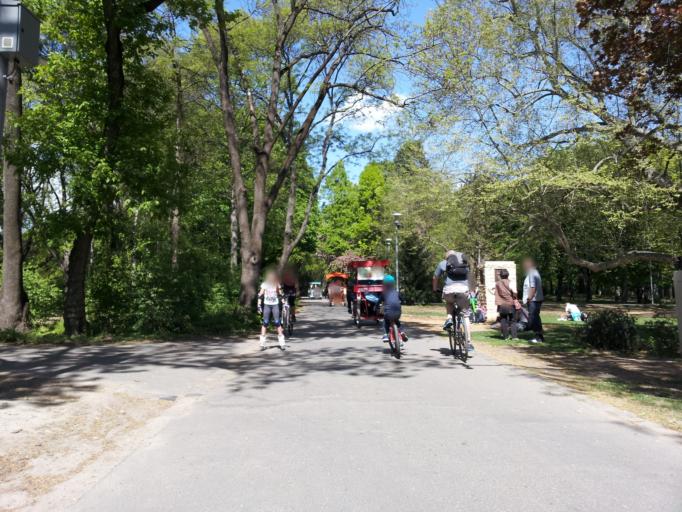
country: HU
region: Budapest
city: Budapest III. keruelet
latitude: 47.5299
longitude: 19.0507
